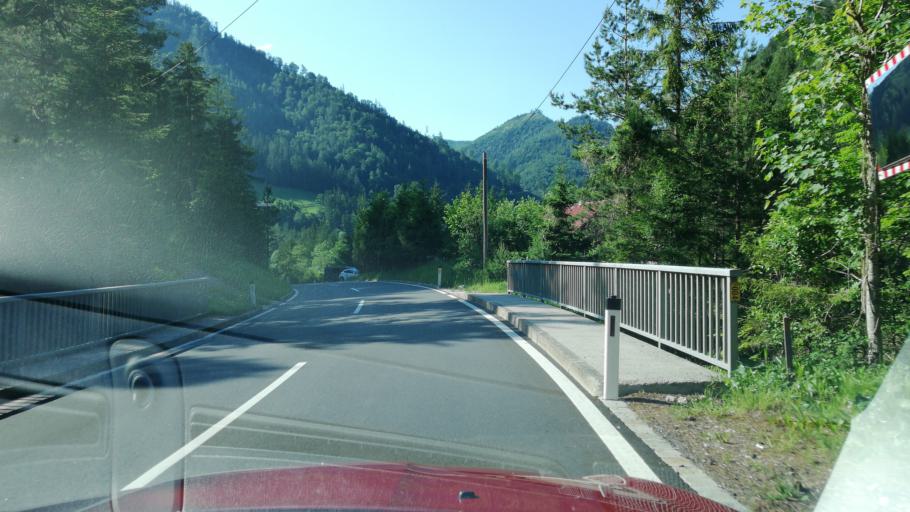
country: AT
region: Upper Austria
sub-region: Politischer Bezirk Kirchdorf an der Krems
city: Rossleithen
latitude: 47.7458
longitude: 14.1661
